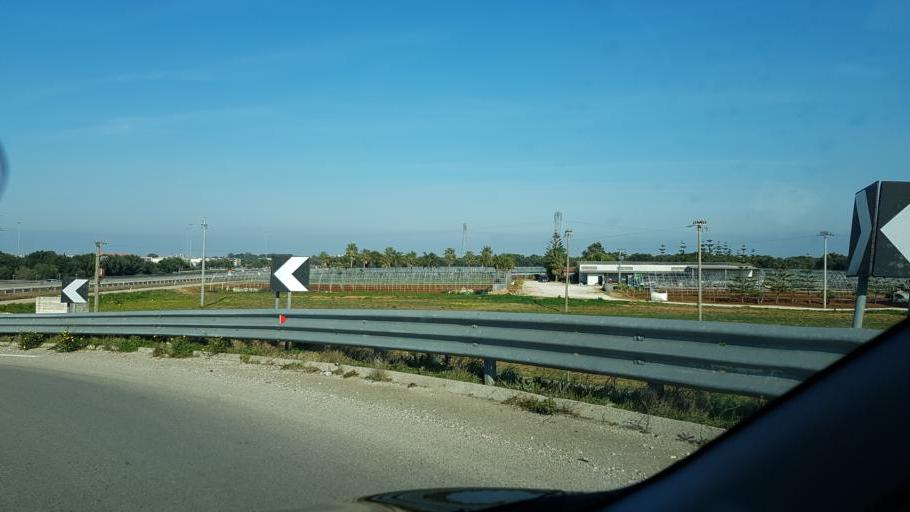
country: IT
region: Apulia
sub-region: Provincia di Brindisi
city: Mesagne
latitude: 40.5750
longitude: 17.8340
